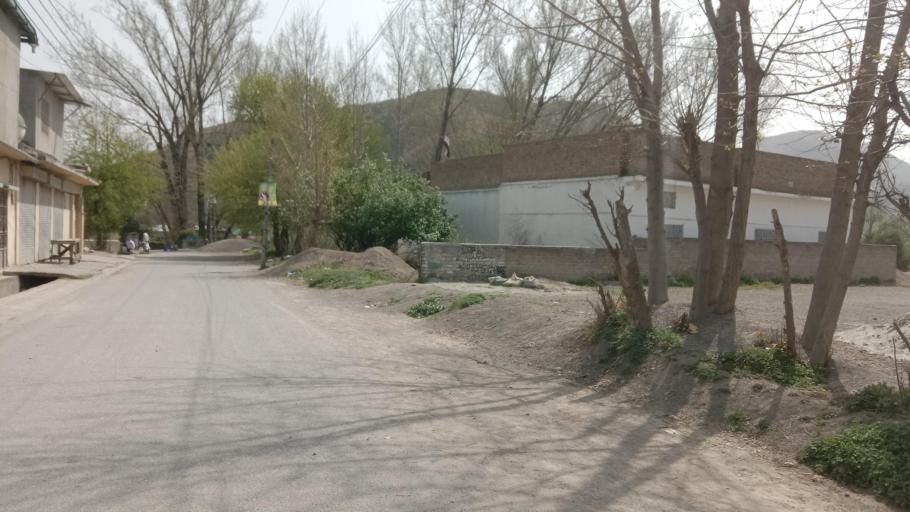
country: PK
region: Khyber Pakhtunkhwa
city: Abbottabad
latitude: 34.1546
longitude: 73.2601
